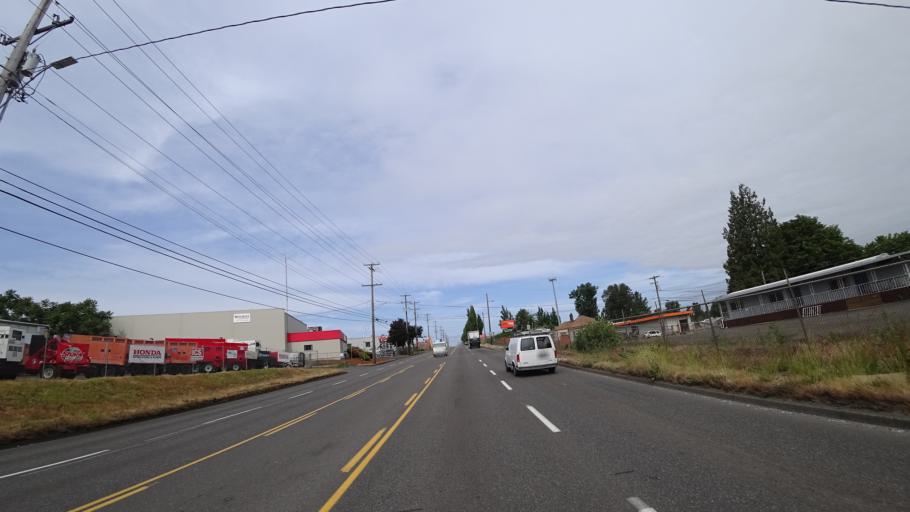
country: US
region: Oregon
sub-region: Multnomah County
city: Portland
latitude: 45.5716
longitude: -122.6196
